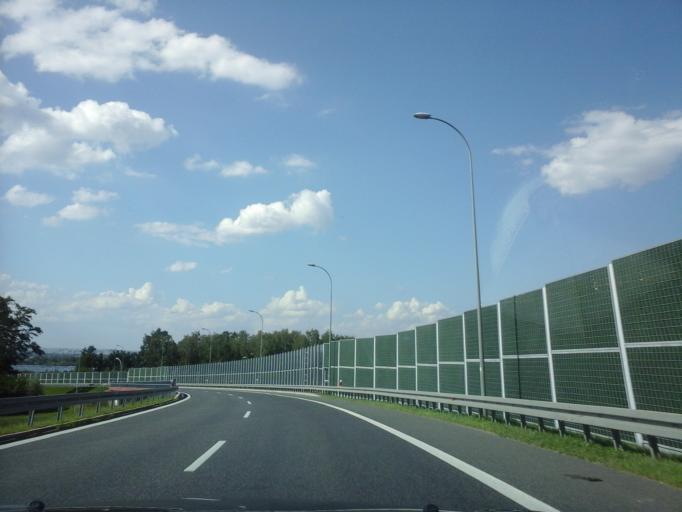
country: PL
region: Lesser Poland Voivodeship
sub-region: Powiat wielicki
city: Czarnochowice
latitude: 50.0135
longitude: 20.0655
